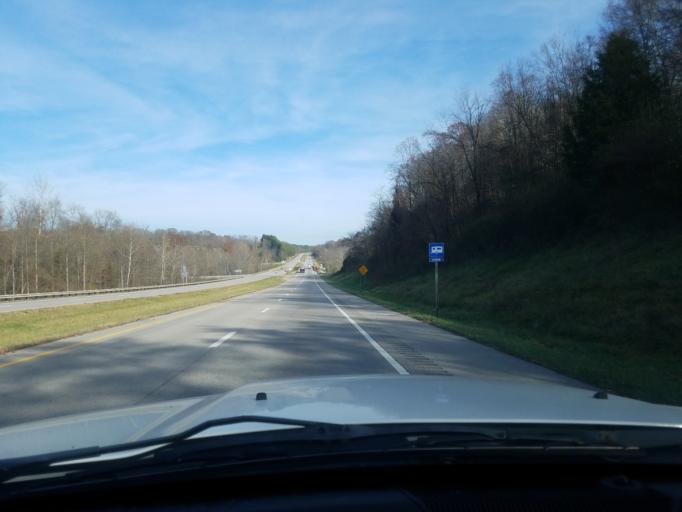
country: US
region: West Virginia
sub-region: Wood County
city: Washington
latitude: 39.2254
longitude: -81.7981
